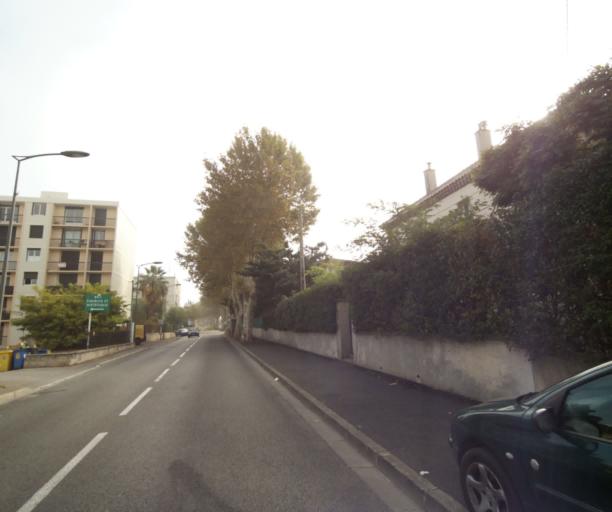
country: FR
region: Provence-Alpes-Cote d'Azur
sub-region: Departement des Bouches-du-Rhone
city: Saint-Victoret
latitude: 43.4196
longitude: 5.2241
